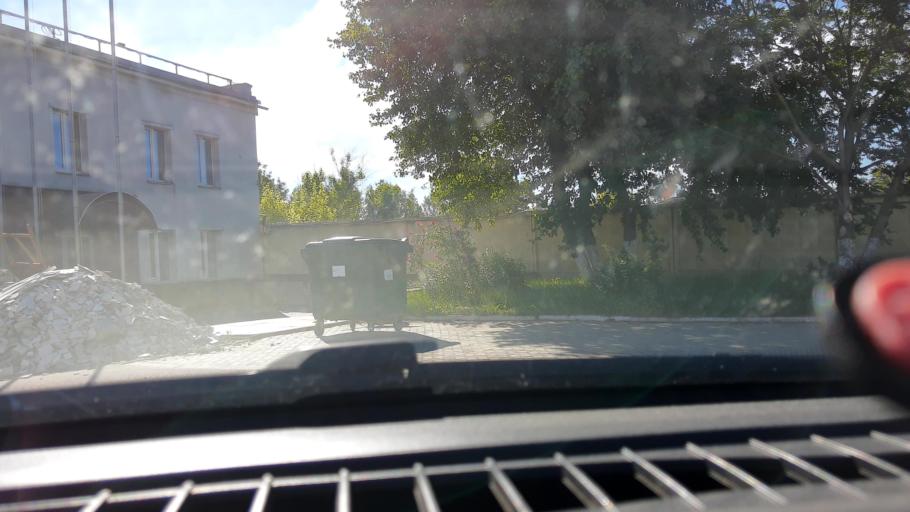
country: RU
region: Nizjnij Novgorod
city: Gorbatovka
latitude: 56.2420
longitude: 43.8742
